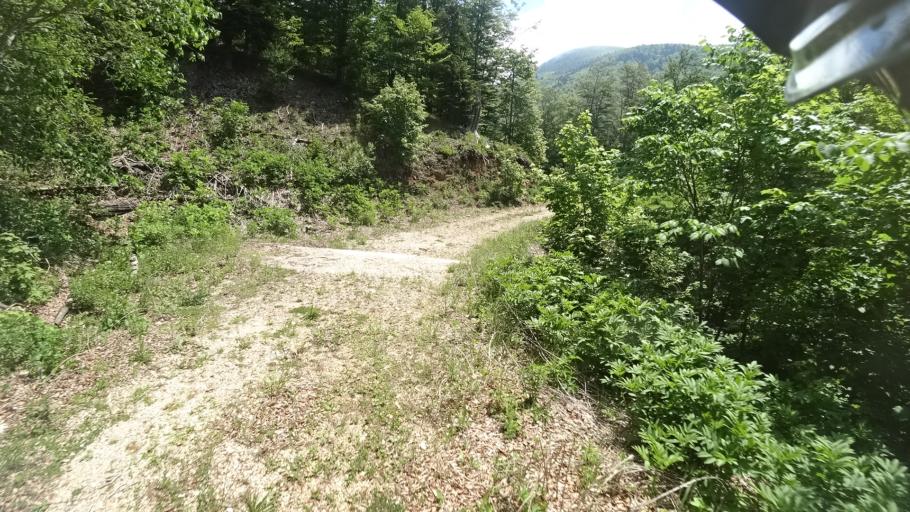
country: BA
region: Federation of Bosnia and Herzegovina
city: Orasac
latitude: 44.5639
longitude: 15.8572
